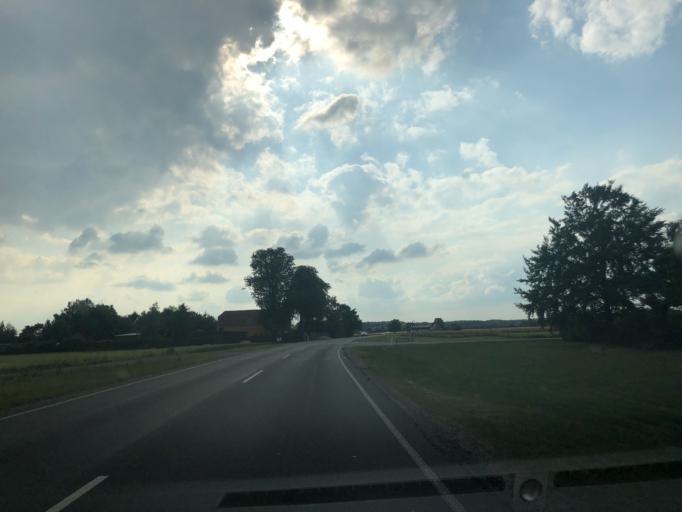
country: DK
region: Zealand
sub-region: Faxe Kommune
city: Fakse
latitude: 55.3140
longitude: 12.1416
